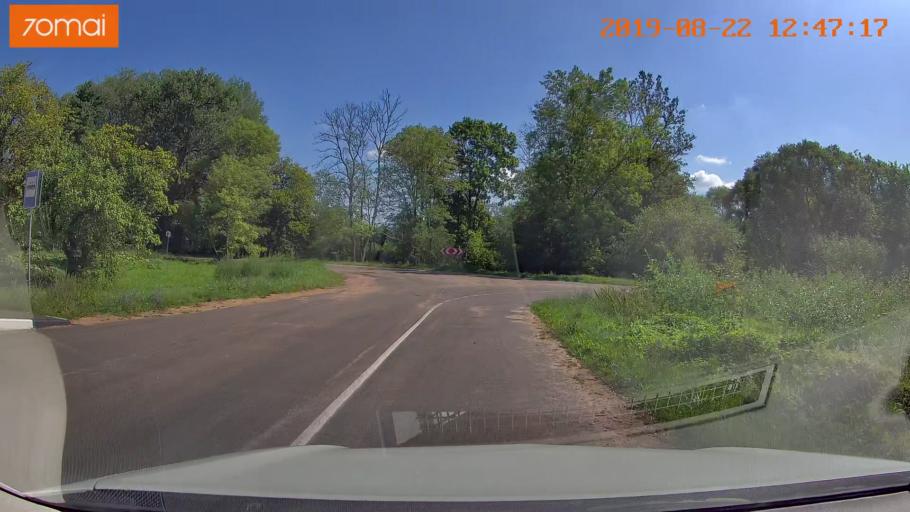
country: BY
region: Minsk
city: Prawdzinski
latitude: 53.4568
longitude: 27.6378
